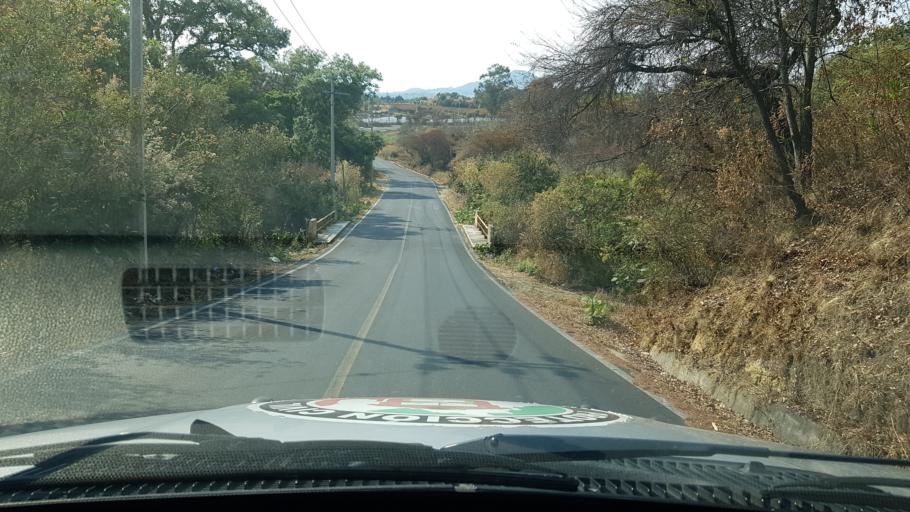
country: MX
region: Mexico
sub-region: Ozumba
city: San Jose Tlacotitlan
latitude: 18.9900
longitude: -98.8226
